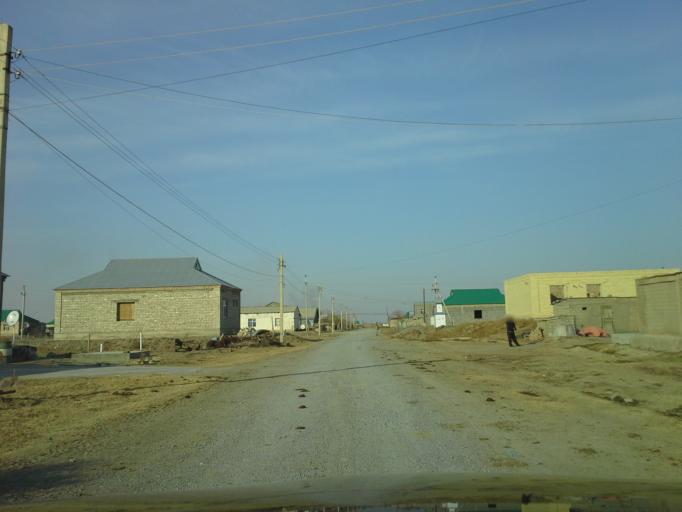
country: TM
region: Ahal
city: Abadan
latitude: 38.1773
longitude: 58.0472
